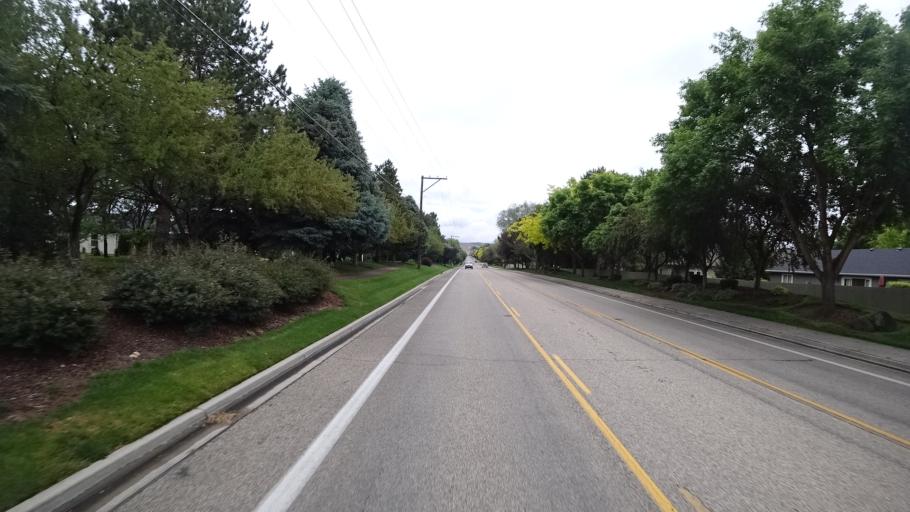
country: US
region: Idaho
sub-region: Ada County
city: Eagle
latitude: 43.7065
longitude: -116.3302
